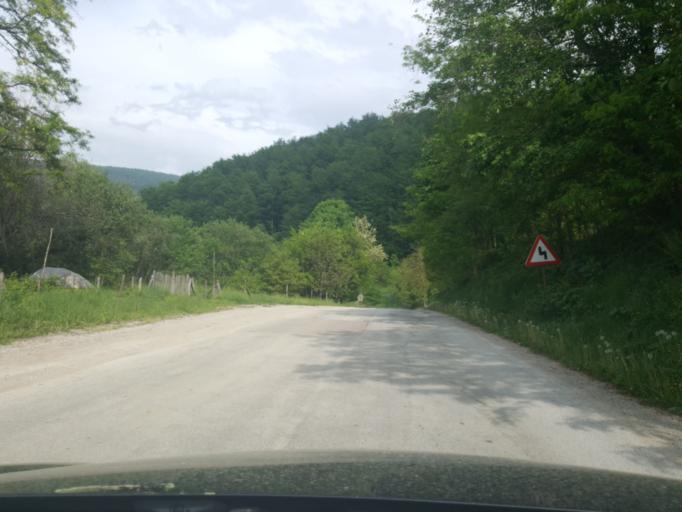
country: RS
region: Central Serbia
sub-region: Zlatiborski Okrug
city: Bajina Basta
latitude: 44.0711
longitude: 19.6551
